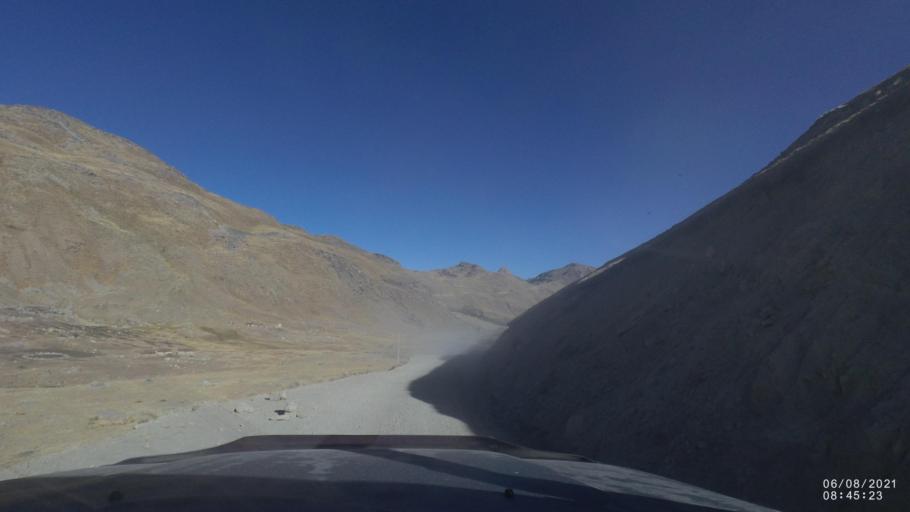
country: BO
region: Cochabamba
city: Sipe Sipe
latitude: -17.1701
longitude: -66.4140
